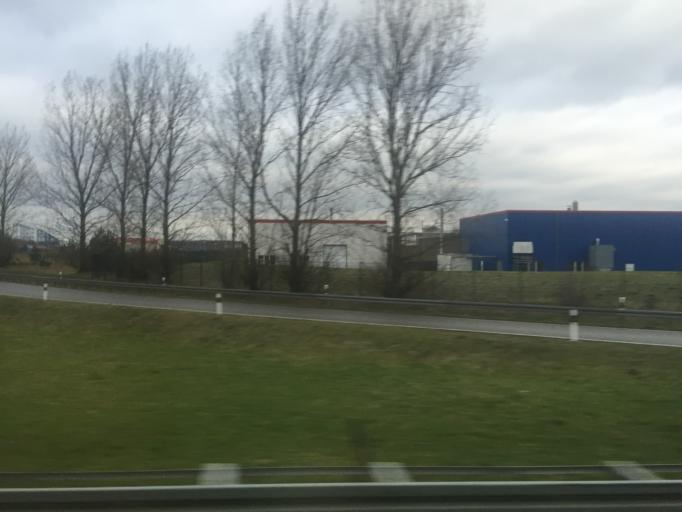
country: DE
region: Mecklenburg-Vorpommern
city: Wittenburg
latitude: 53.4977
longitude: 11.0987
